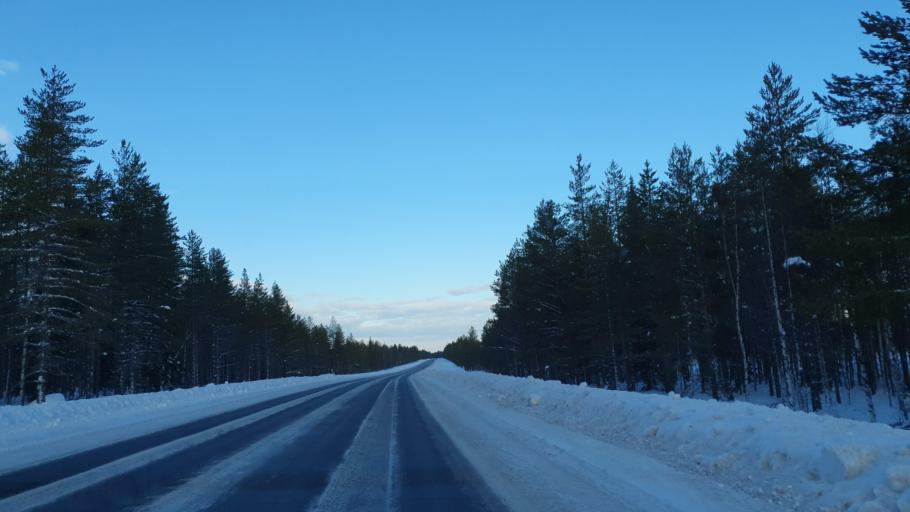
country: FI
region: Kainuu
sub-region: Kajaani
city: Vaala
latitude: 64.5828
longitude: 26.8255
